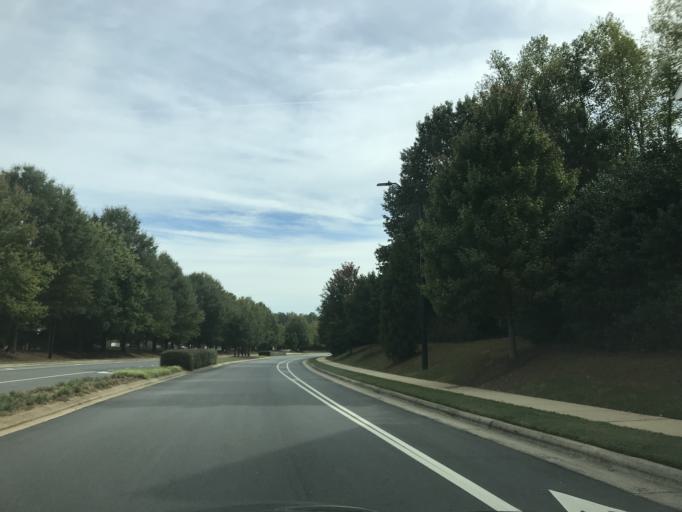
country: US
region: North Carolina
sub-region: Wake County
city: Wake Forest
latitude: 35.9623
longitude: -78.5480
